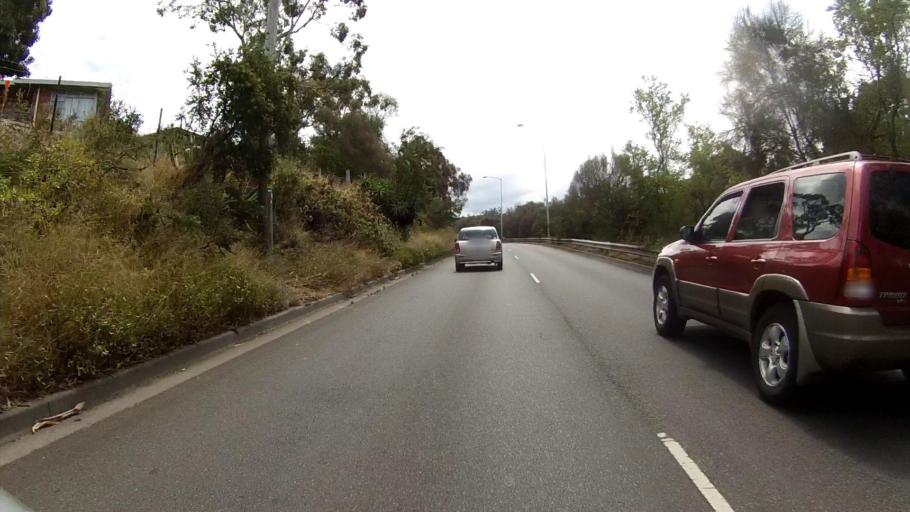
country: AU
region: Tasmania
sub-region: Clarence
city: Bellerive
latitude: -42.8654
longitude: 147.3650
